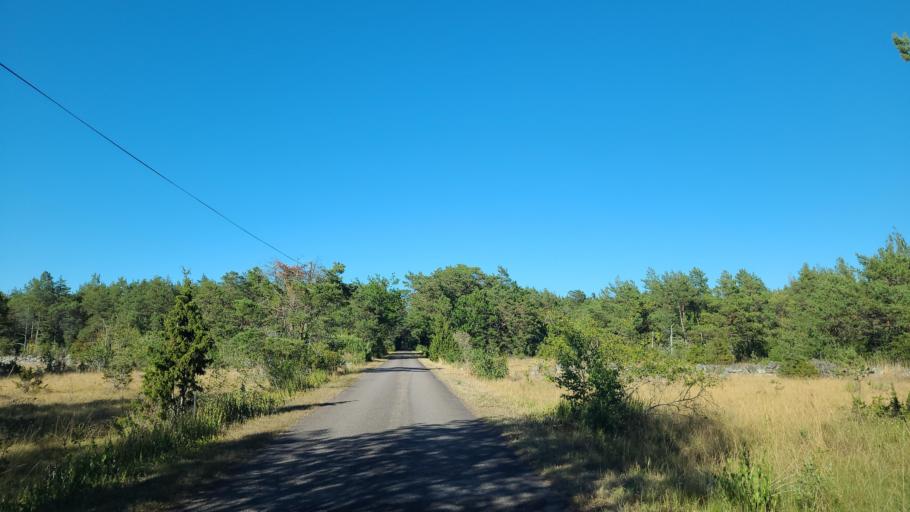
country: SE
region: Kalmar
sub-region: Borgholms Kommun
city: Borgholm
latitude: 57.3196
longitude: 17.0566
